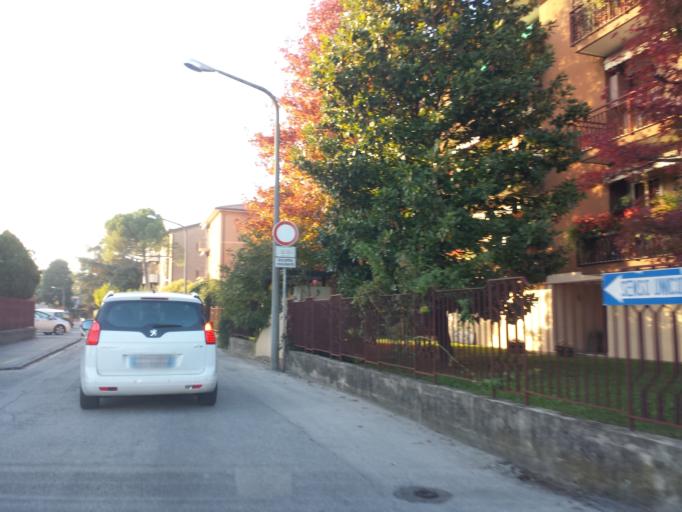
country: IT
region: Veneto
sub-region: Provincia di Vicenza
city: Vicenza
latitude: 45.5736
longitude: 11.5445
